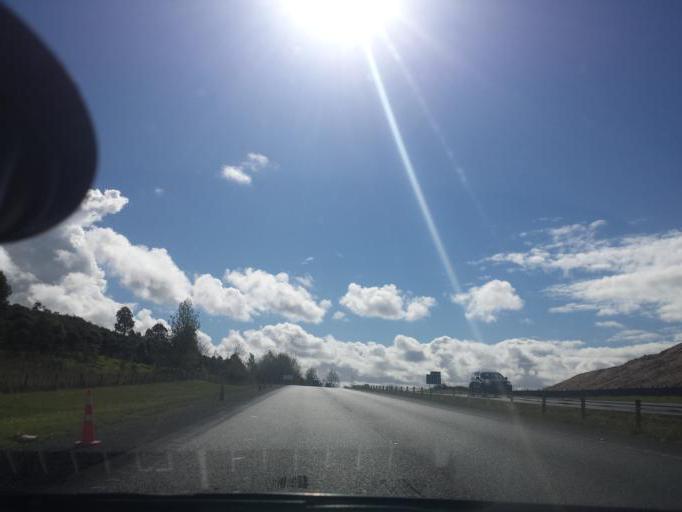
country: NZ
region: Auckland
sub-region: Auckland
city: Rothesay Bay
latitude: -36.6151
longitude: 174.6618
